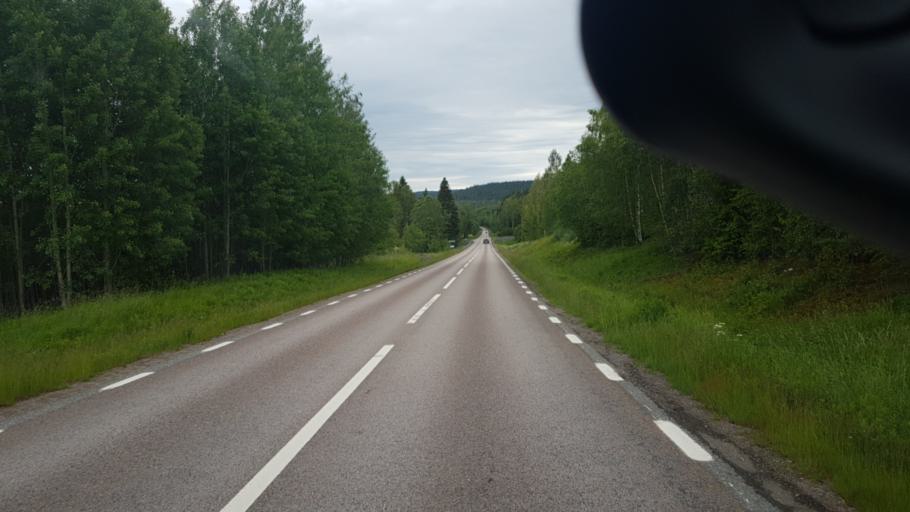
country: SE
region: Vaermland
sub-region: Eda Kommun
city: Amotfors
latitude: 59.7239
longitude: 12.2809
